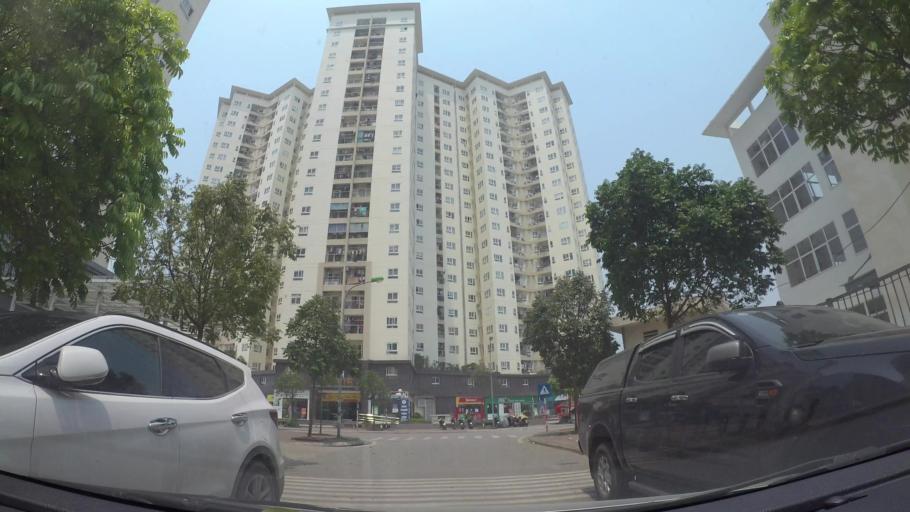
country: VN
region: Ha Noi
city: Thanh Xuan
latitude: 20.9946
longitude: 105.7791
